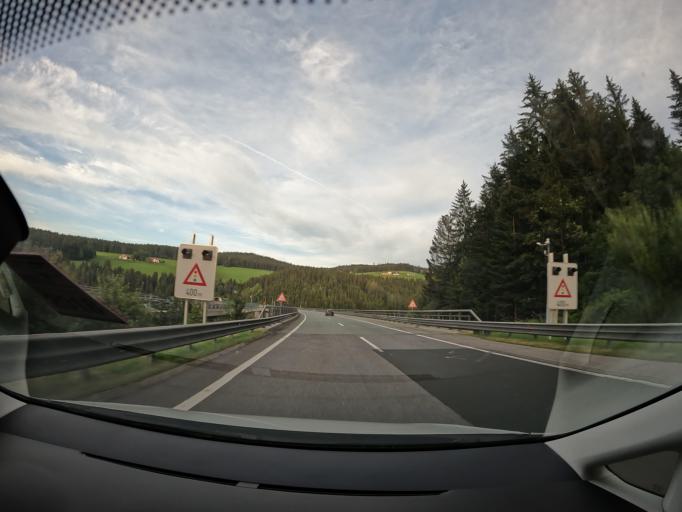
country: AT
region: Styria
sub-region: Politischer Bezirk Voitsberg
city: Pack
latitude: 46.9160
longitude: 14.9921
